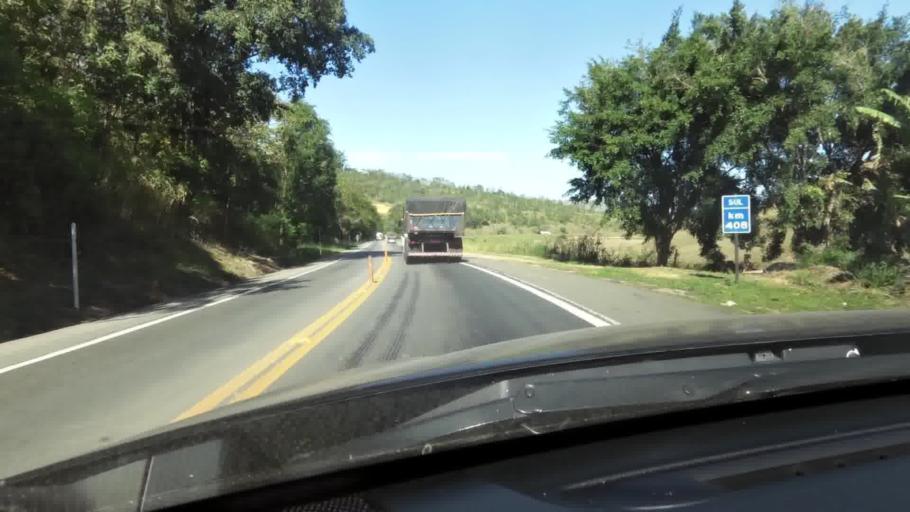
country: BR
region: Espirito Santo
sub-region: Cachoeiro De Itapemirim
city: Cachoeiro de Itapemirim
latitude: -20.8905
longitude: -41.0387
